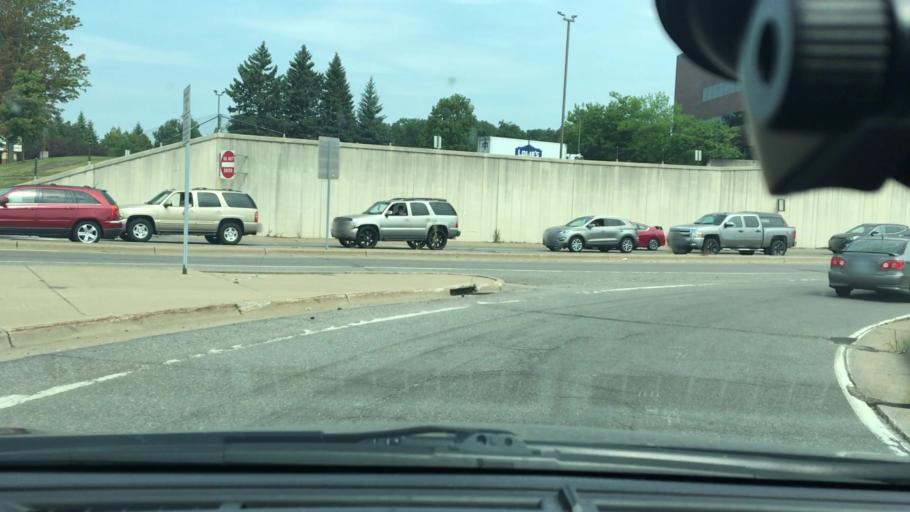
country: US
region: Minnesota
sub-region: Hennepin County
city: Minnetonka Mills
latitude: 44.9720
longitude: -93.4454
